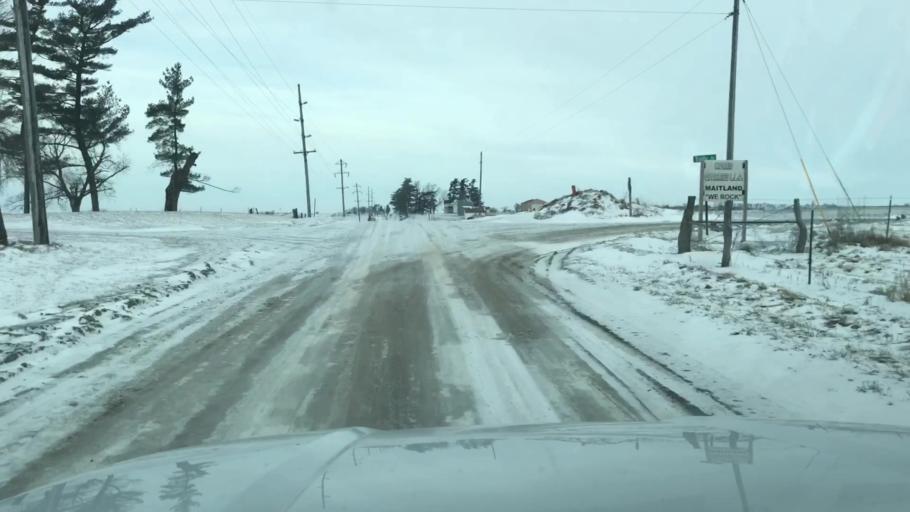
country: US
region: Missouri
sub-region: Holt County
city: Oregon
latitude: 40.1301
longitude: -95.0693
